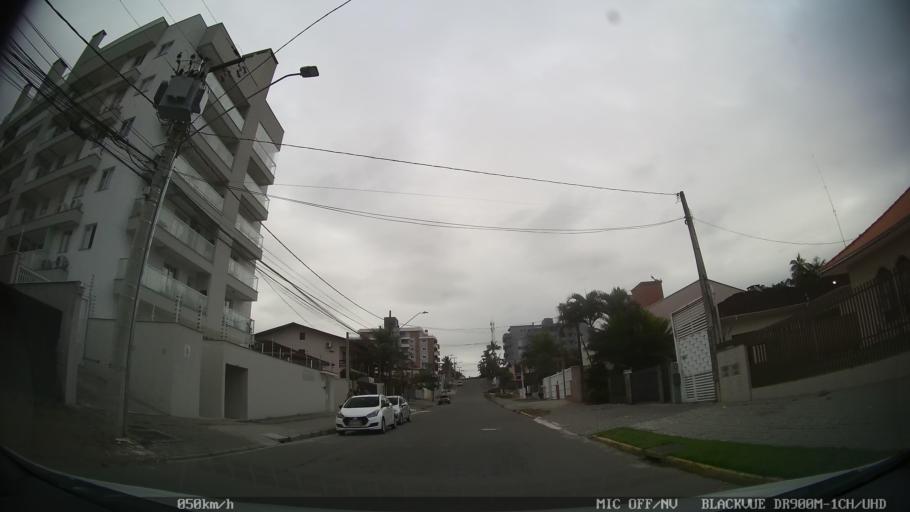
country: BR
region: Santa Catarina
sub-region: Joinville
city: Joinville
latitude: -26.2756
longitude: -48.8806
